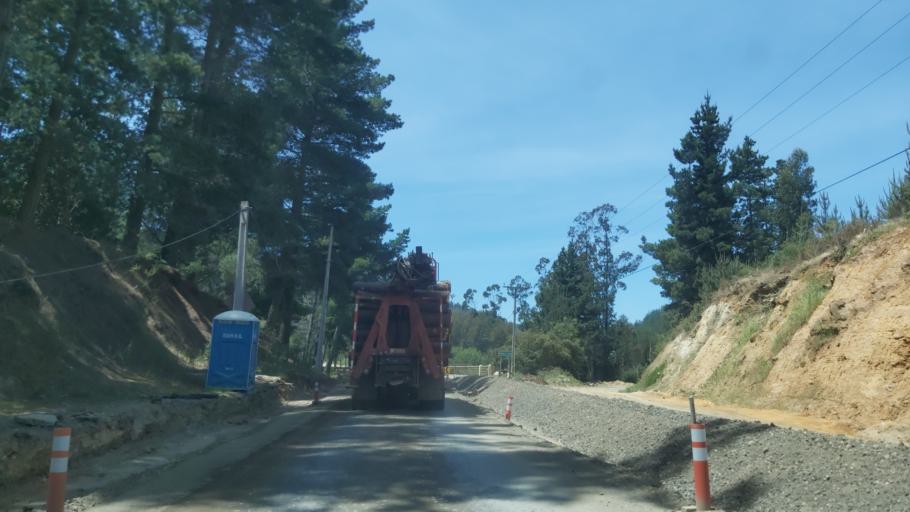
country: CL
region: Maule
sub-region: Provincia de Talca
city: Constitucion
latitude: -35.4481
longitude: -72.4707
